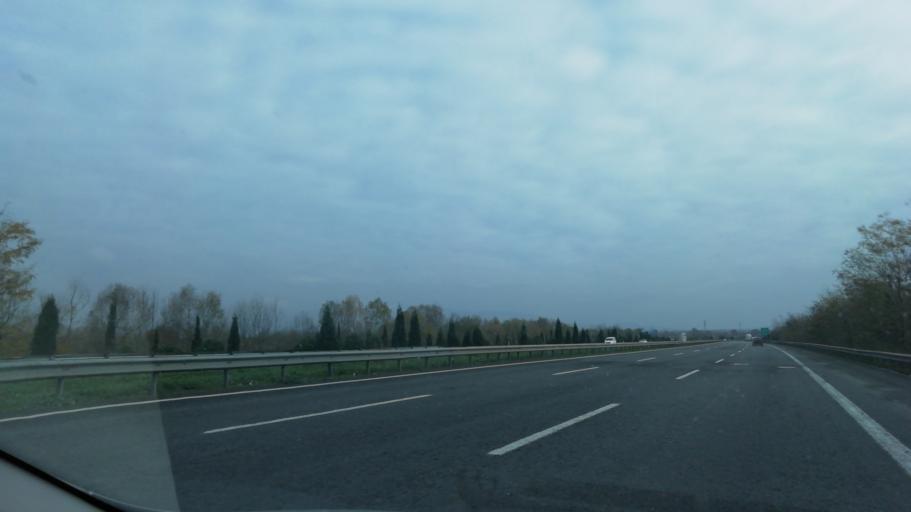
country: TR
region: Sakarya
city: Akyazi
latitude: 40.7459
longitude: 30.6761
